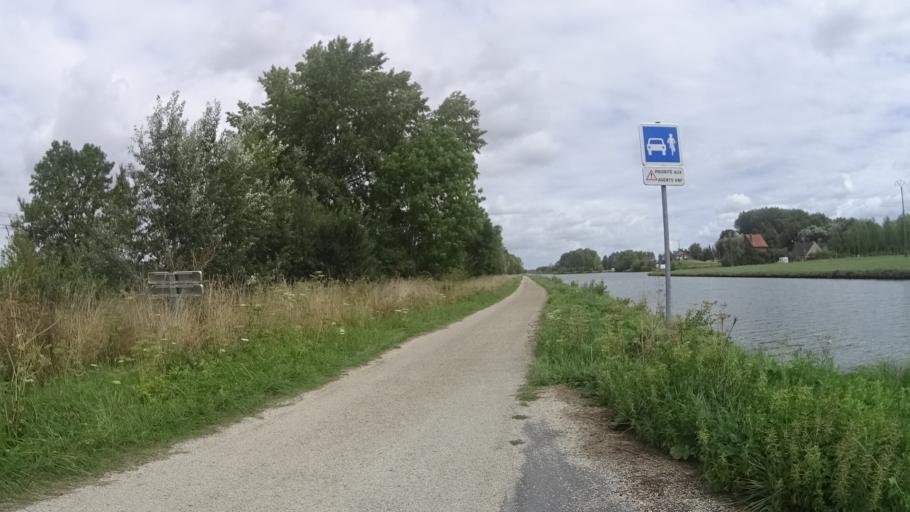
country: FR
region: Picardie
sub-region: Departement de l'Aisne
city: Ognes
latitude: 49.5913
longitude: 3.1860
